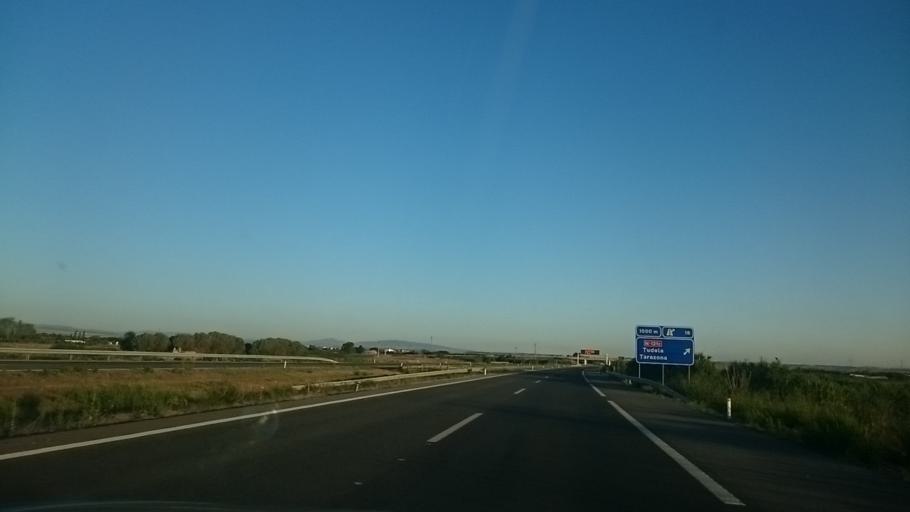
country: ES
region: Navarre
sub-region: Provincia de Navarra
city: Murchante
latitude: 42.0204
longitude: -1.6182
